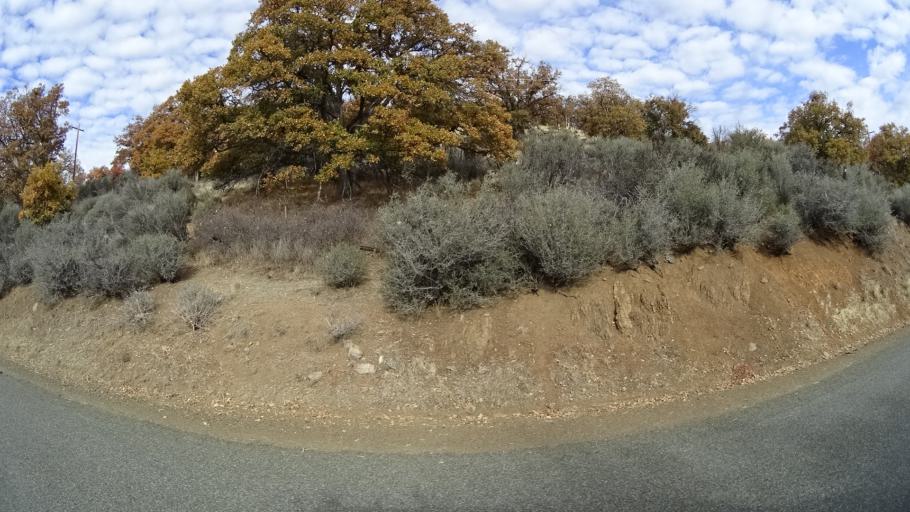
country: US
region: California
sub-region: Siskiyou County
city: Yreka
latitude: 41.6265
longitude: -122.7771
